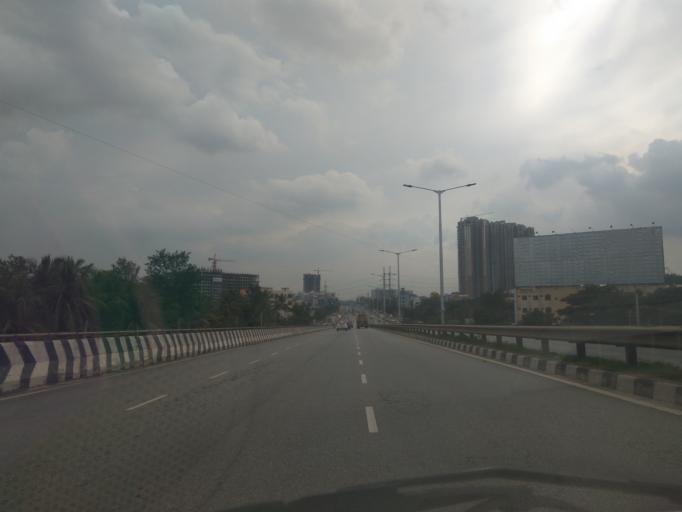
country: IN
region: Karnataka
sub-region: Bangalore Rural
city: Hoskote
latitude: 13.0252
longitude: 77.7188
